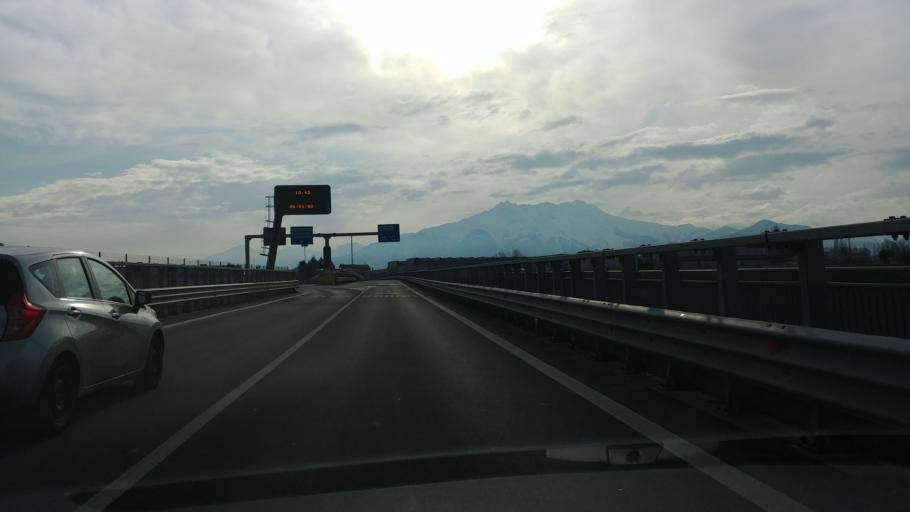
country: IT
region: Piedmont
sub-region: Provincia di Cuneo
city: Cuneo
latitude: 44.3830
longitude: 7.5251
